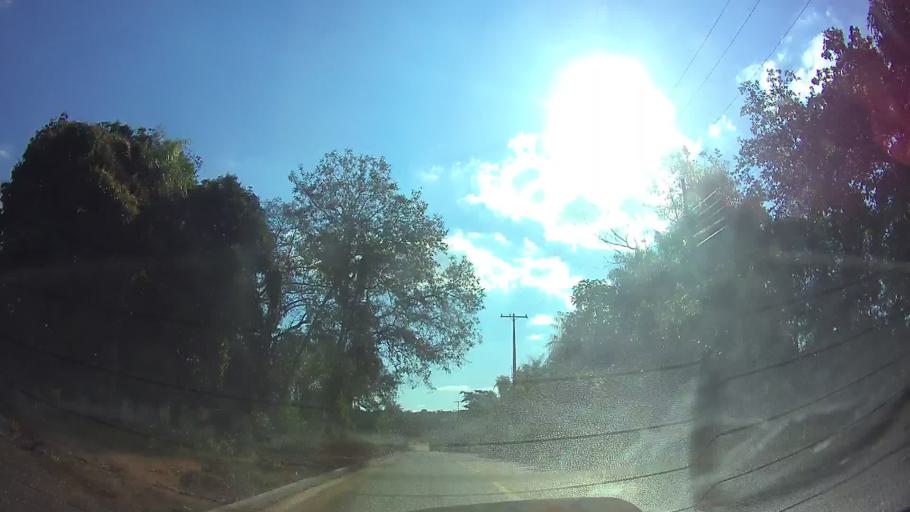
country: PY
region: Central
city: Aregua
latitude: -25.2746
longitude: -57.4422
